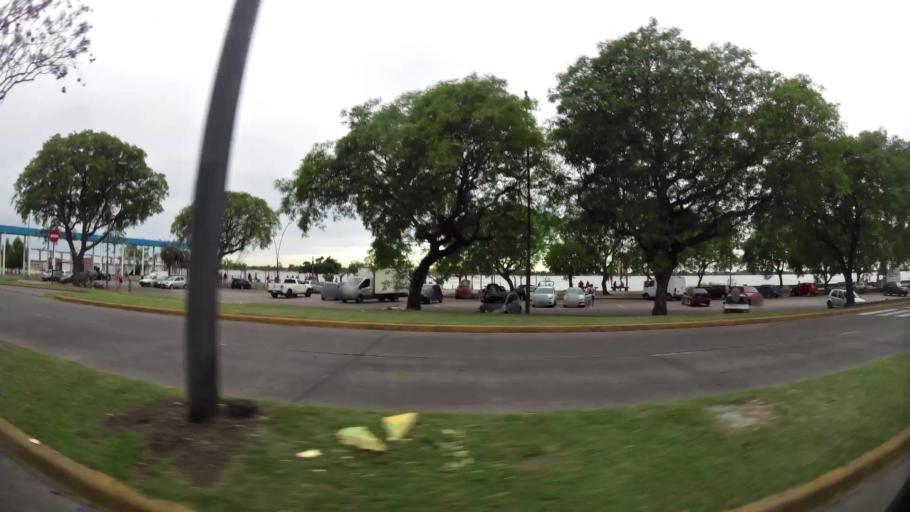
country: AR
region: Santa Fe
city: Granadero Baigorria
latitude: -32.8853
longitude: -60.6878
